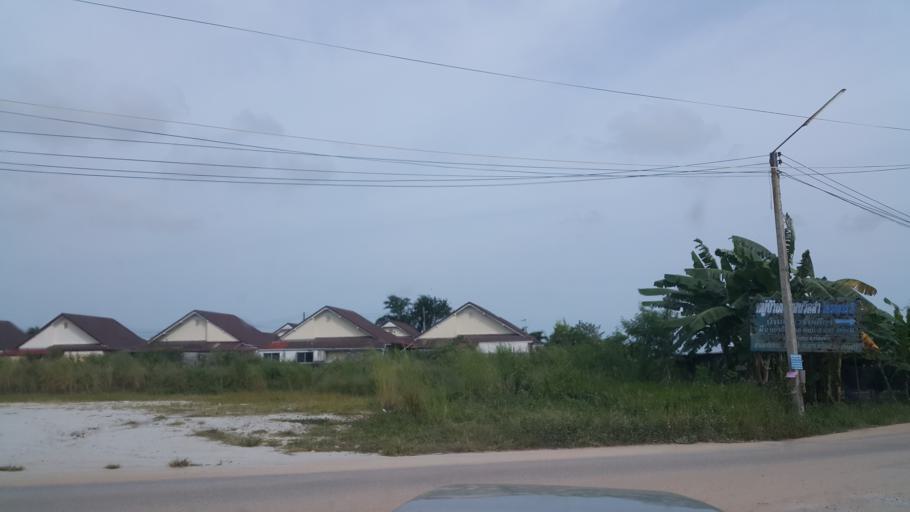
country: TH
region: Rayong
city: Ban Chang
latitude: 12.7254
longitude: 101.0623
